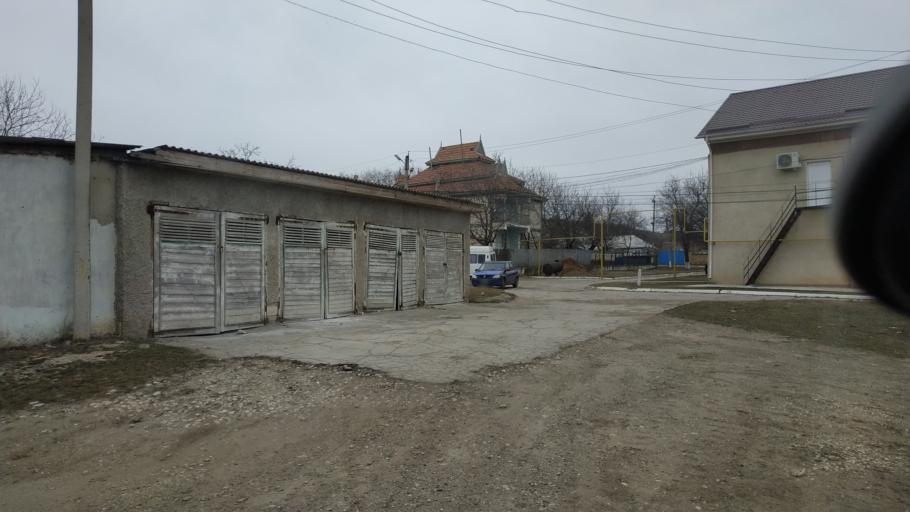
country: MD
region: Telenesti
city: Cocieri
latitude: 47.3795
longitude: 29.1191
